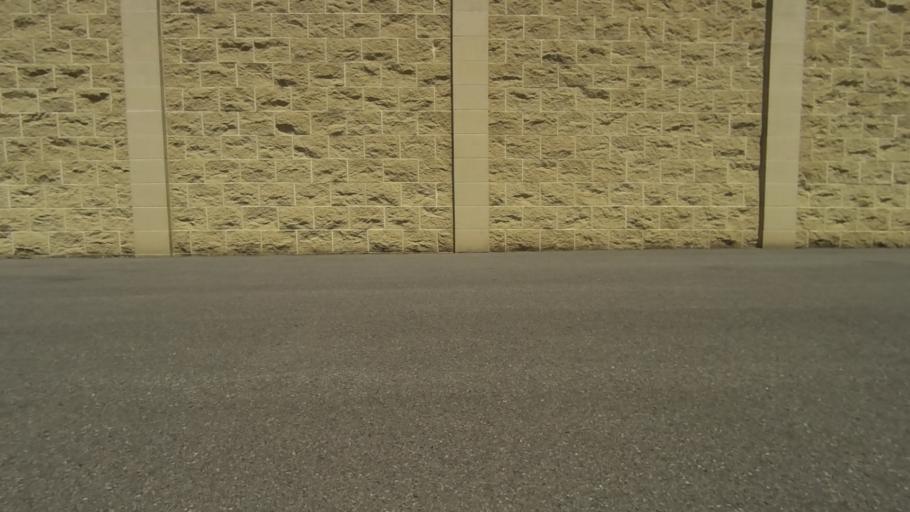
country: US
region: Pennsylvania
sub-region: Centre County
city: State College
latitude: 40.8118
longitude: -77.8575
